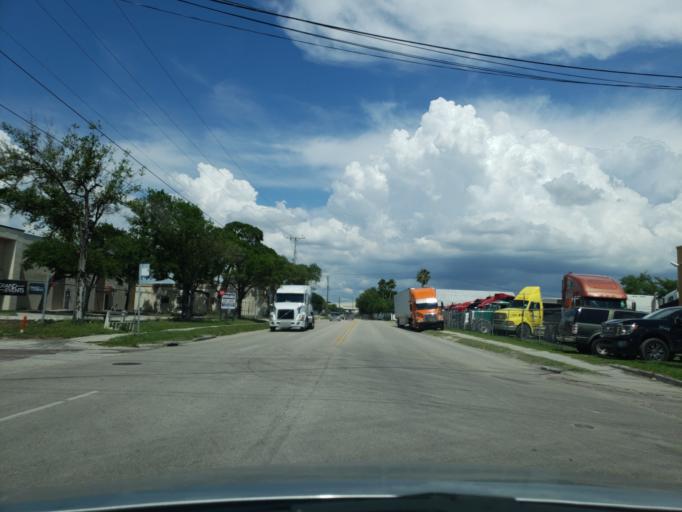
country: US
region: Florida
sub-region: Hillsborough County
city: East Lake-Orient Park
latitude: 27.9602
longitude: -82.4101
